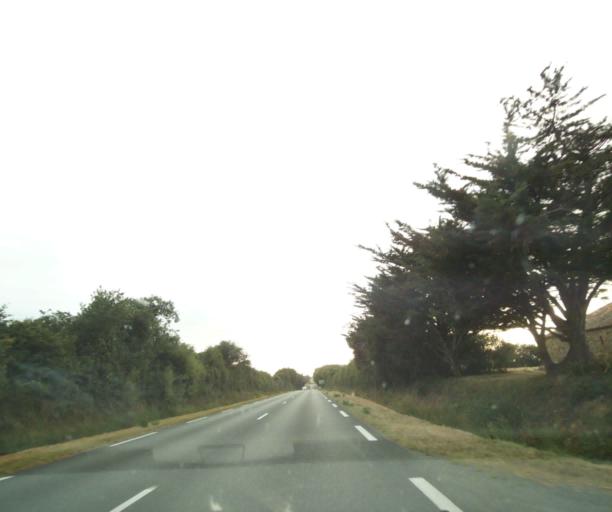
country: FR
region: Pays de la Loire
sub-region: Departement de la Vendee
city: Chateau-d'Olonne
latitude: 46.4795
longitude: -1.6954
